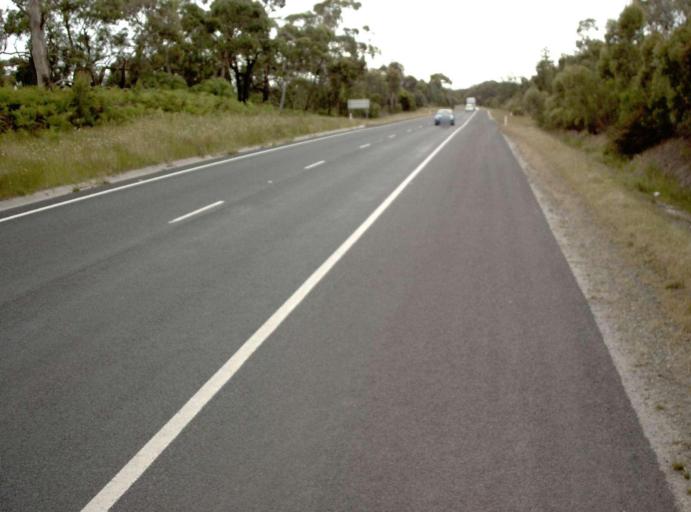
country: AU
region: Victoria
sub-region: Bass Coast
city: North Wonthaggi
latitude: -38.4302
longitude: 145.5032
